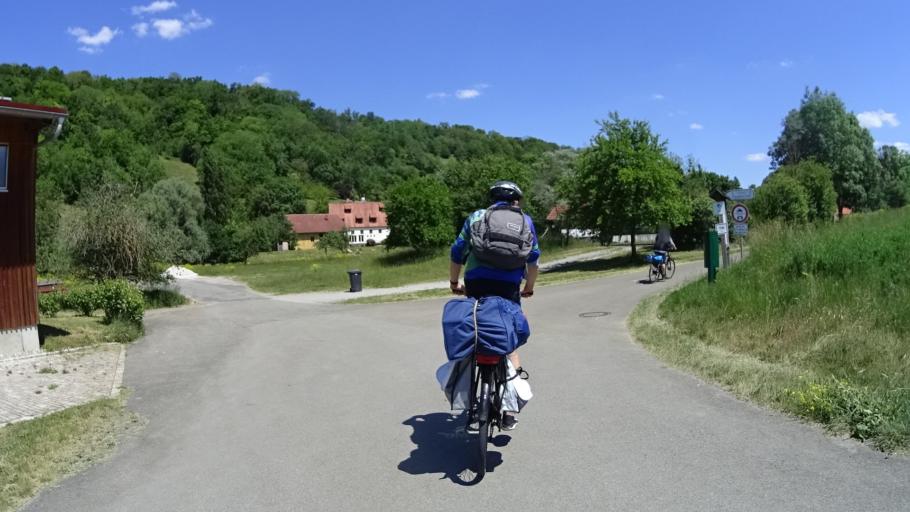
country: DE
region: Bavaria
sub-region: Regierungsbezirk Mittelfranken
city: Adelshofen
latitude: 49.4470
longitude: 10.1107
